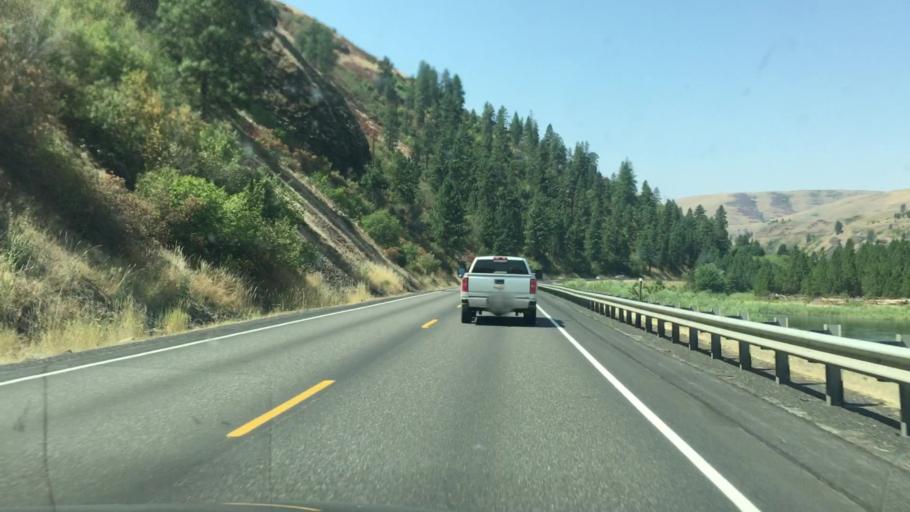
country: US
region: Idaho
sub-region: Nez Perce County
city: Lapwai
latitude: 46.4886
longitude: -116.7345
